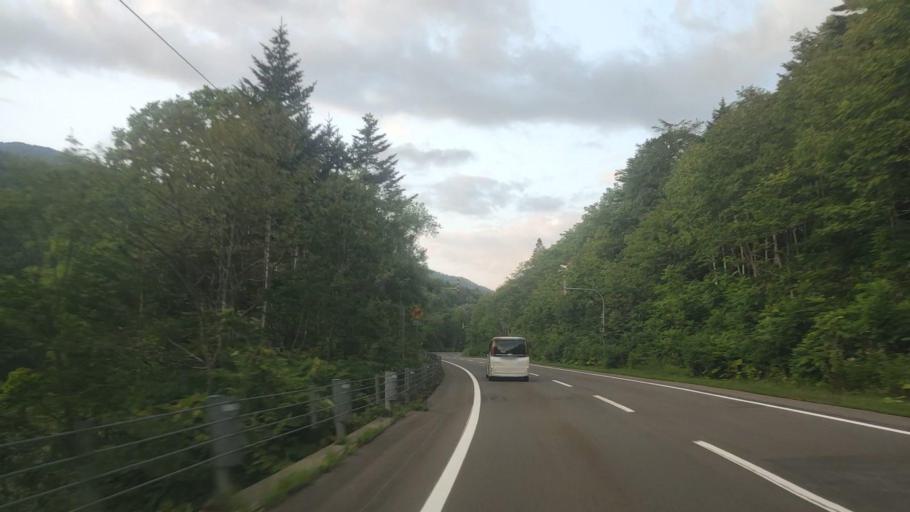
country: JP
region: Hokkaido
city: Ashibetsu
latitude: 43.3085
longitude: 142.1286
